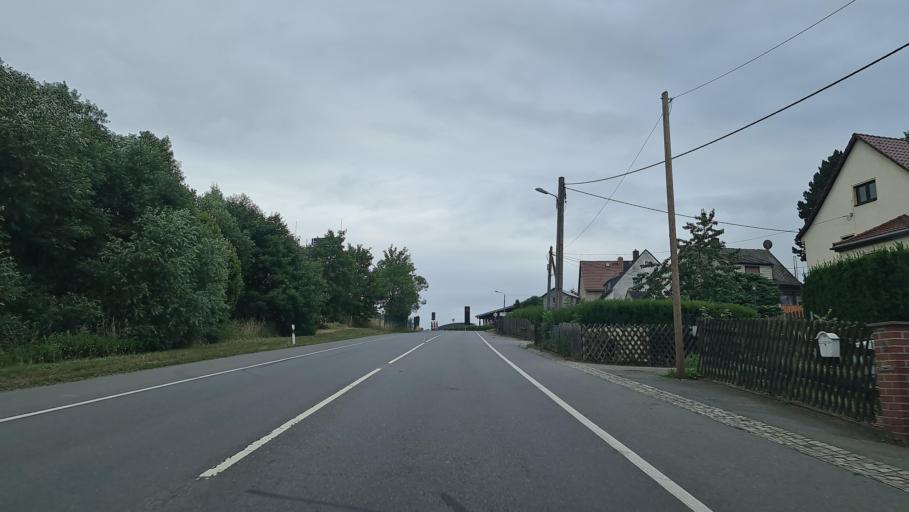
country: DE
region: Saxony
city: Oberlungwitz
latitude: 50.7896
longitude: 12.6820
